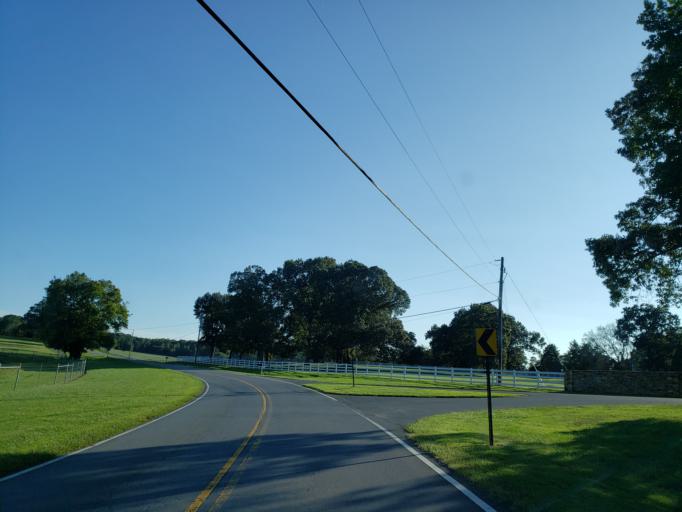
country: US
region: Georgia
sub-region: Bartow County
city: Rydal
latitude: 34.3125
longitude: -84.7737
